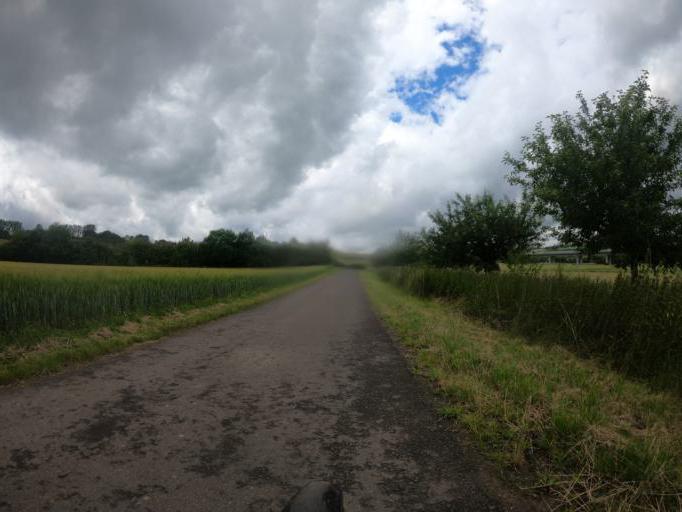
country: DE
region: Hesse
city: Hessisch Lichtenau
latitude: 51.1902
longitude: 9.7828
